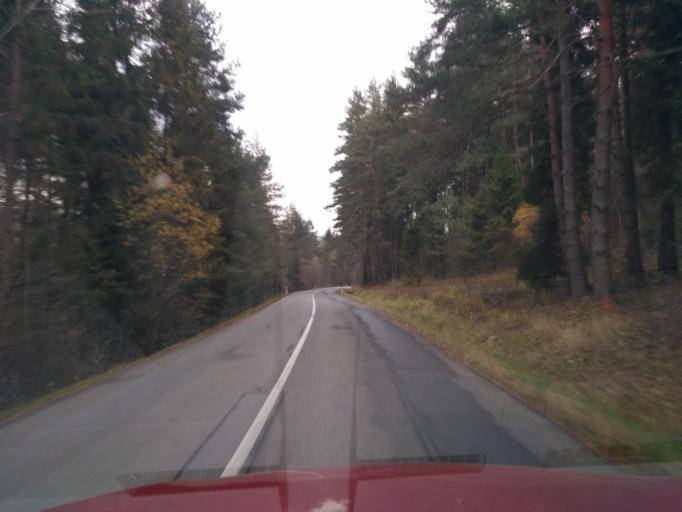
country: SK
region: Kosicky
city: Medzev
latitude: 48.7930
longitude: 20.7819
